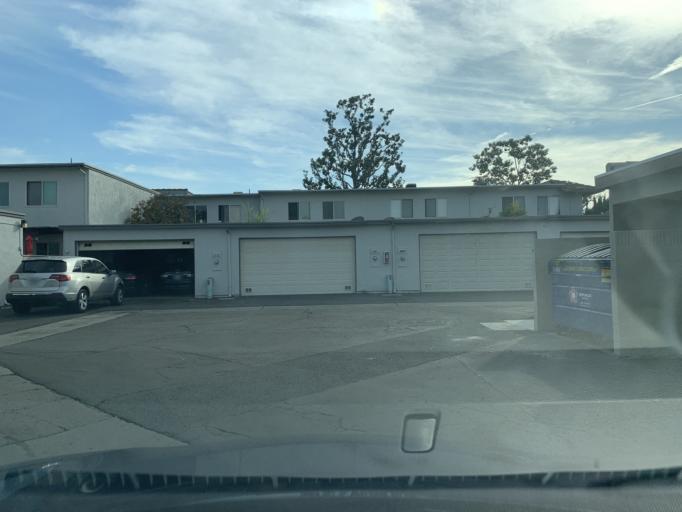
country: US
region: California
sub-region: Orange County
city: Garden Grove
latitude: 33.7942
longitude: -117.9406
